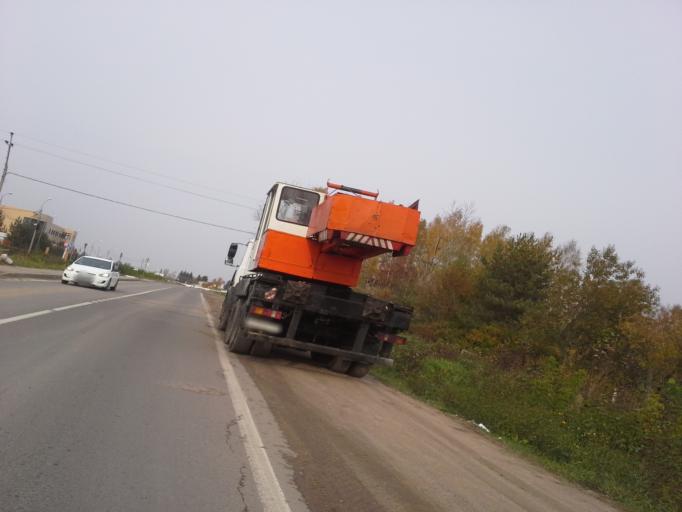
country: RU
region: Moskovskaya
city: Bol'shiye Vyazemy
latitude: 55.6309
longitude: 37.0048
